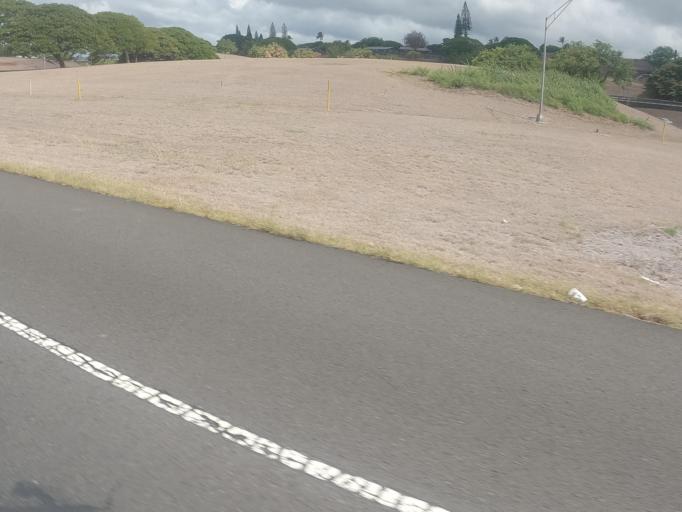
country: US
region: Hawaii
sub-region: Honolulu County
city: Halawa
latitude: 21.3726
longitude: -157.9242
